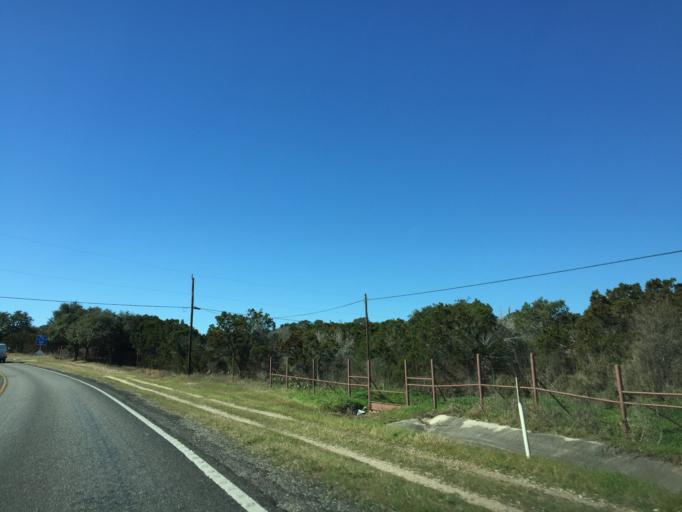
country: US
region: Texas
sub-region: Comal County
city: Garden Ridge
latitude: 29.6939
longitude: -98.3306
